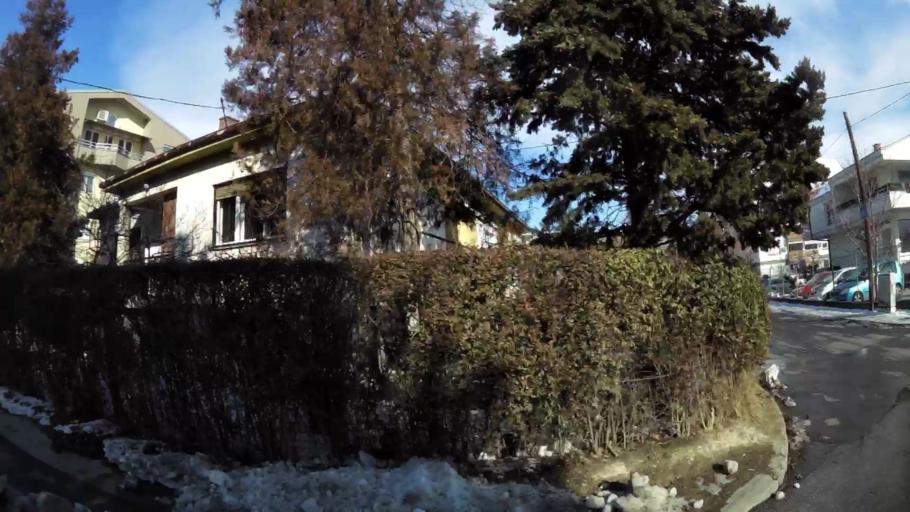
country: MK
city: Krushopek
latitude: 42.0042
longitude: 21.3695
